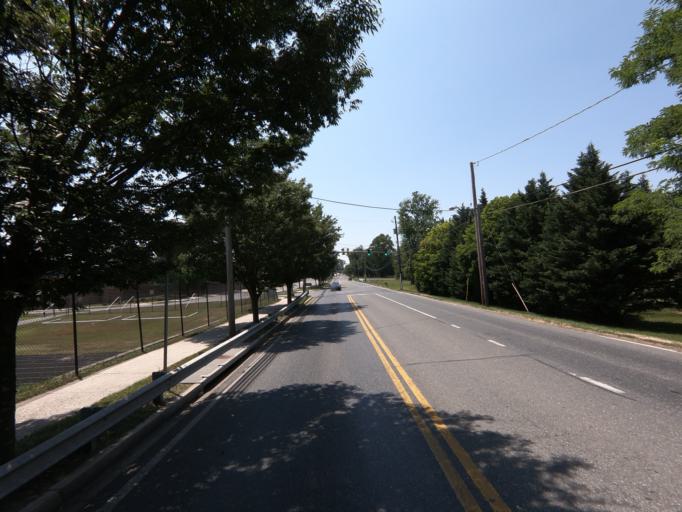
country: US
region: Maryland
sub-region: Montgomery County
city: Ashton-Sandy Spring
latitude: 39.1491
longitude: -77.0168
